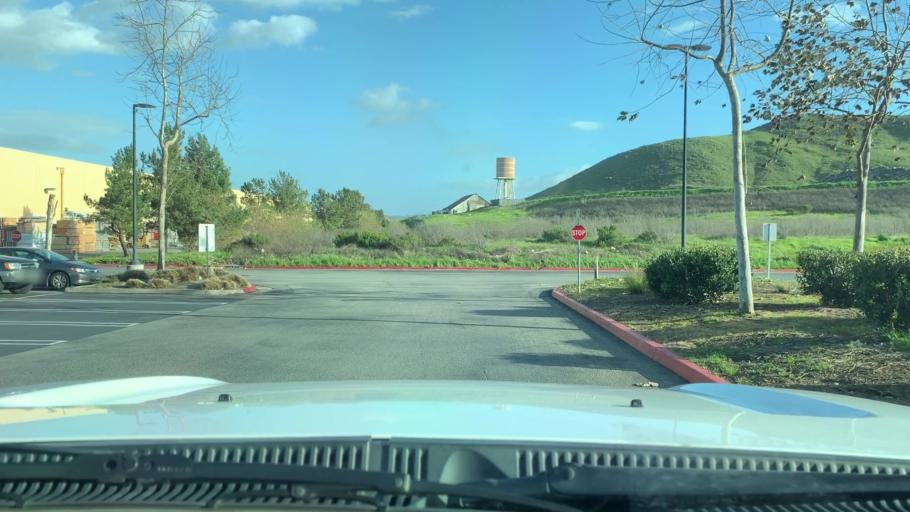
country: US
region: California
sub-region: San Luis Obispo County
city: San Luis Obispo
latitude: 35.2510
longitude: -120.6912
